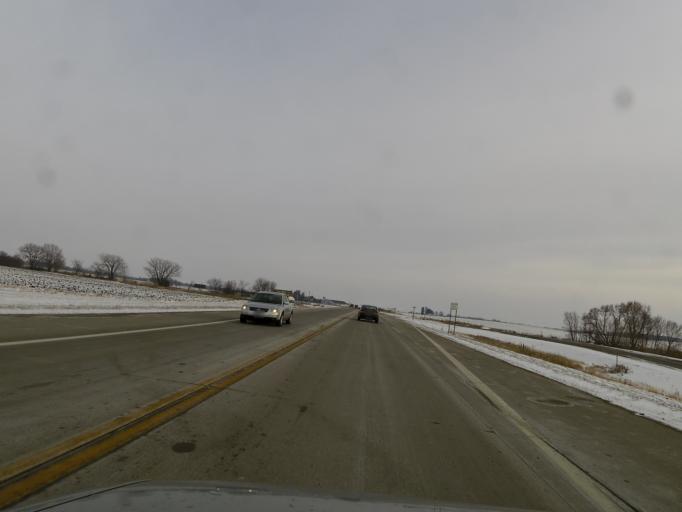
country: US
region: Minnesota
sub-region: McLeod County
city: Hutchinson
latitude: 44.8948
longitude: -94.3223
